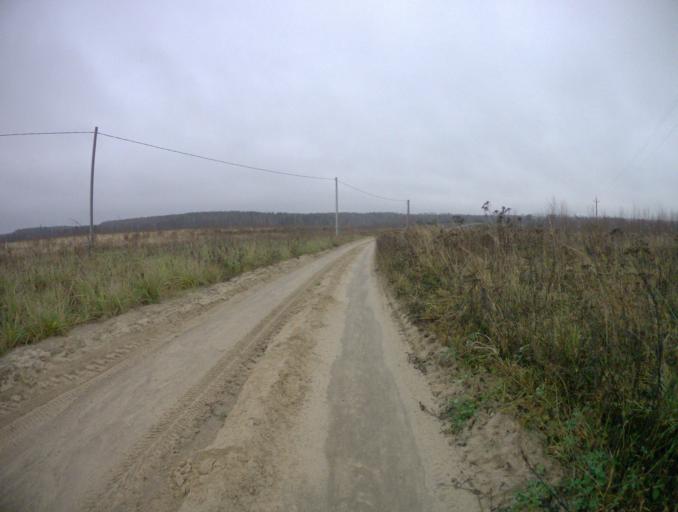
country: RU
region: Vladimir
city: Golovino
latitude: 55.9789
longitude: 40.4539
